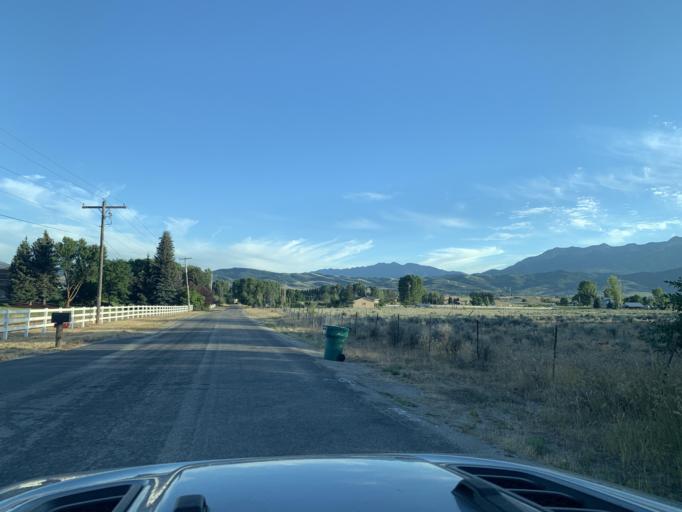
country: US
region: Utah
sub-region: Weber County
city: Wolf Creek
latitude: 41.2867
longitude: -111.7583
